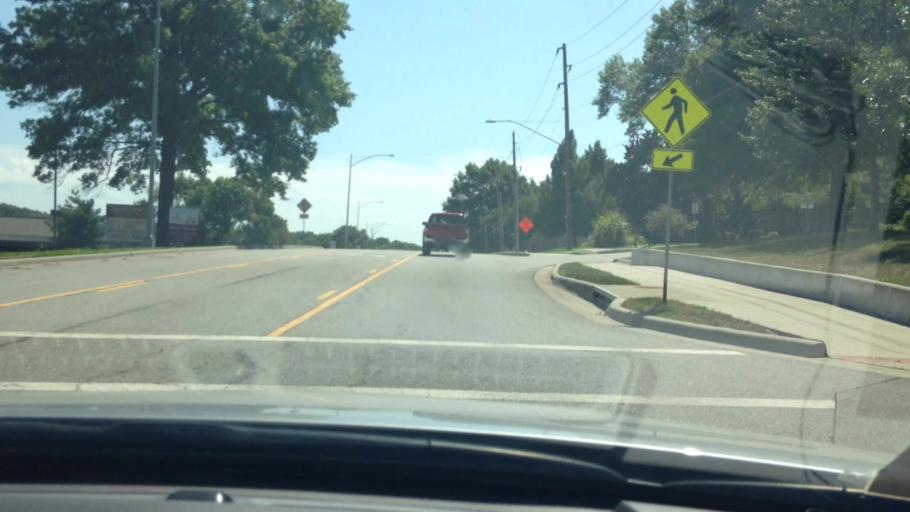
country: US
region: Kansas
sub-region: Johnson County
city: Mission
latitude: 39.0185
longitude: -94.6491
